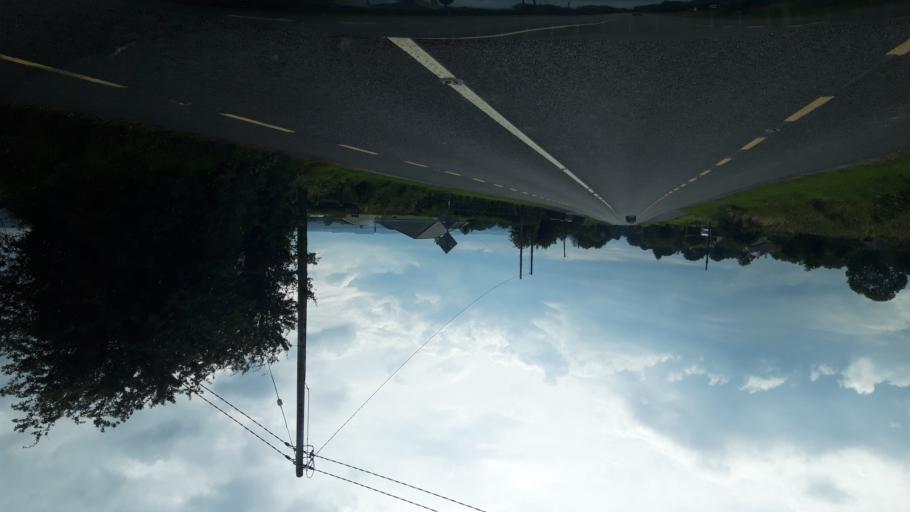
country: IE
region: Leinster
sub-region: Kilkenny
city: Castlecomer
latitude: 52.8402
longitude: -7.1402
